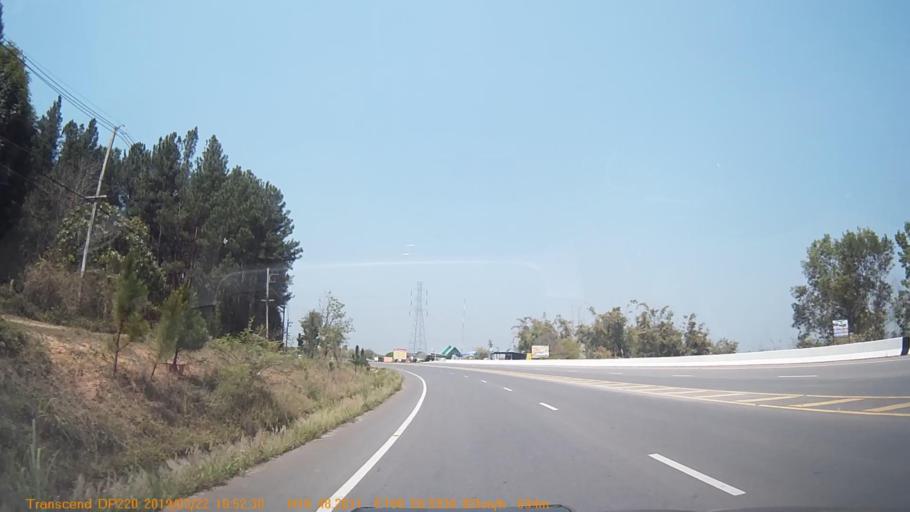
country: TH
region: Phetchabun
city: Khao Kho
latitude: 16.8044
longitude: 100.9762
